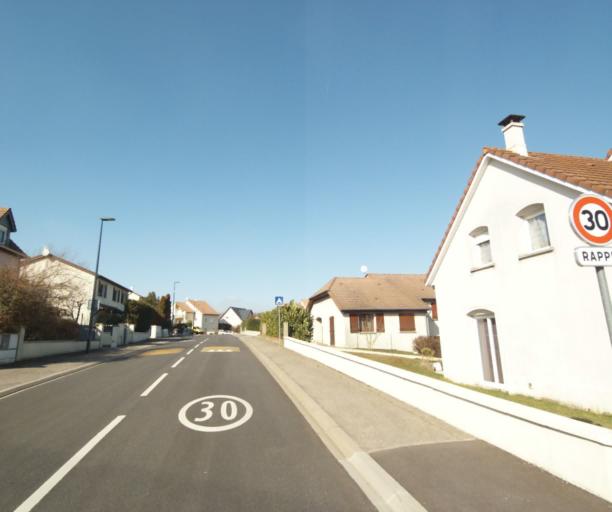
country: FR
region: Lorraine
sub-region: Departement de Meurthe-et-Moselle
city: Vandoeuvre-les-Nancy
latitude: 48.6398
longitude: 6.1770
